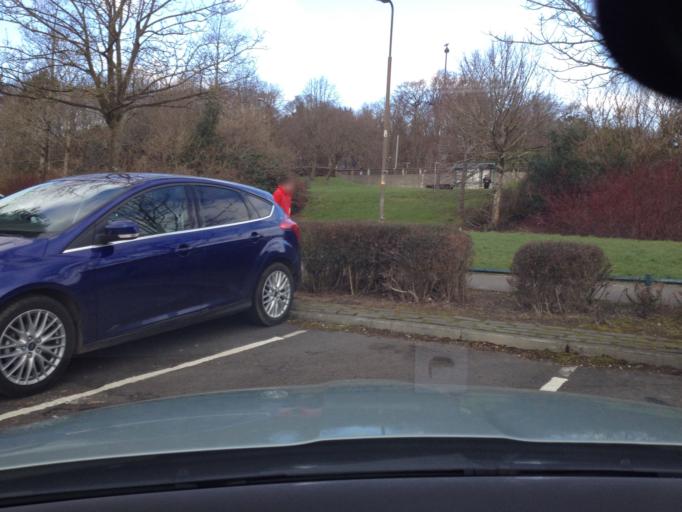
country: GB
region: Scotland
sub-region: West Lothian
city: Livingston
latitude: 55.8991
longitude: -3.5031
